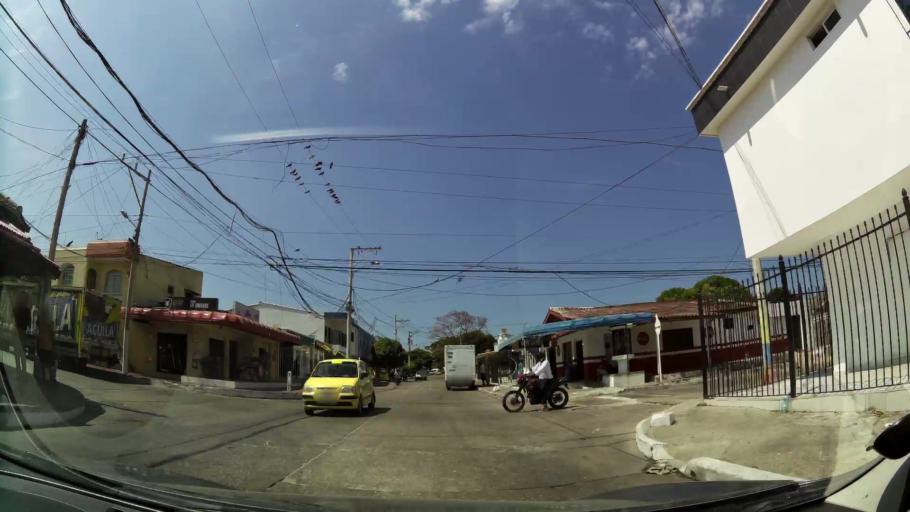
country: CO
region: Atlantico
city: Barranquilla
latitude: 10.9637
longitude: -74.8031
